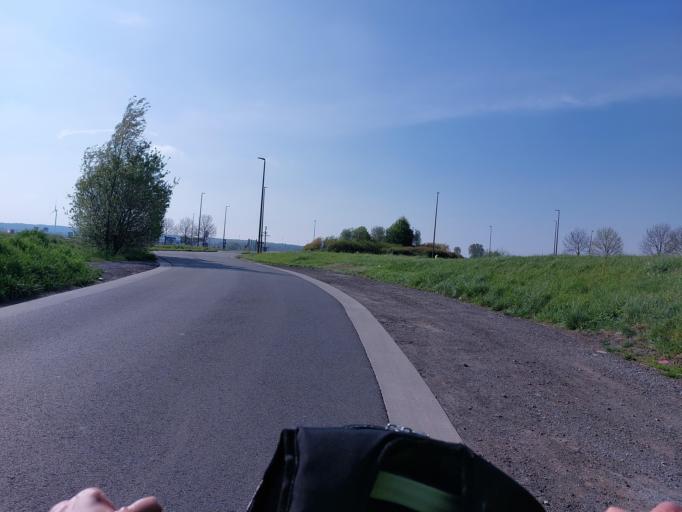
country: BE
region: Wallonia
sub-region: Province du Hainaut
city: Ecaussinnes-d'Enghien
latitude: 50.5481
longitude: 4.1478
